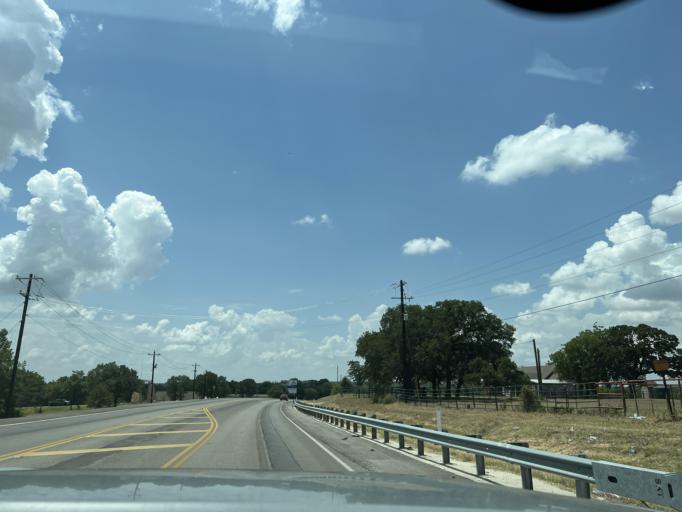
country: US
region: Texas
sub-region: Parker County
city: Weatherford
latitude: 32.8128
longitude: -97.7781
